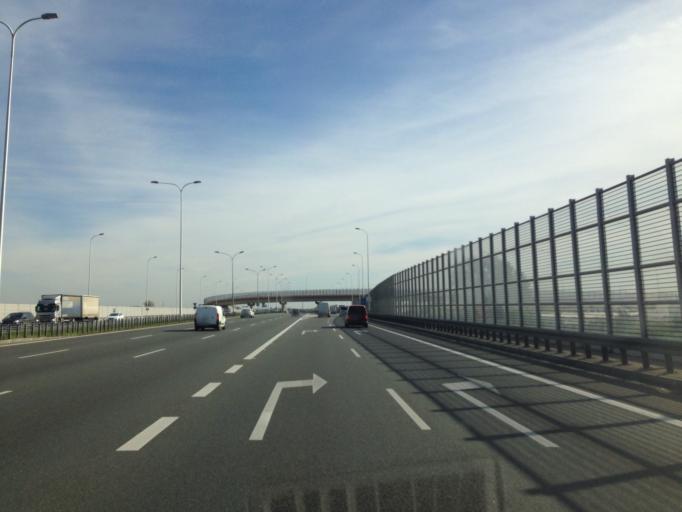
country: PL
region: Masovian Voivodeship
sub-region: Powiat pruszkowski
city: Michalowice
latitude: 52.1825
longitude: 20.8786
